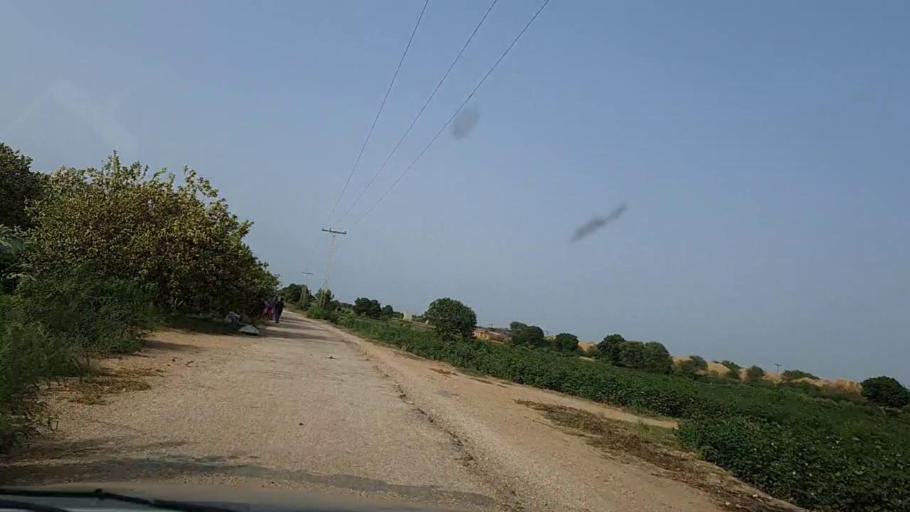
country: PK
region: Sindh
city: Kotri
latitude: 25.2307
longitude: 68.2577
